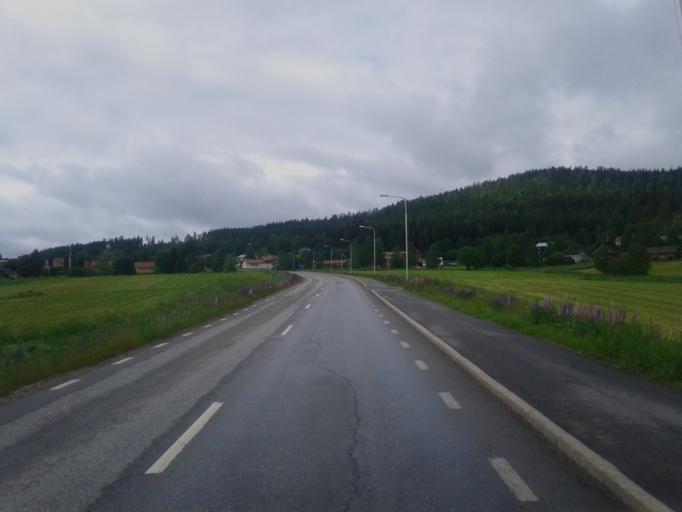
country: SE
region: Gaevleborg
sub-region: Hudiksvalls Kommun
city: Delsbo
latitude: 62.1057
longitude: 16.7185
